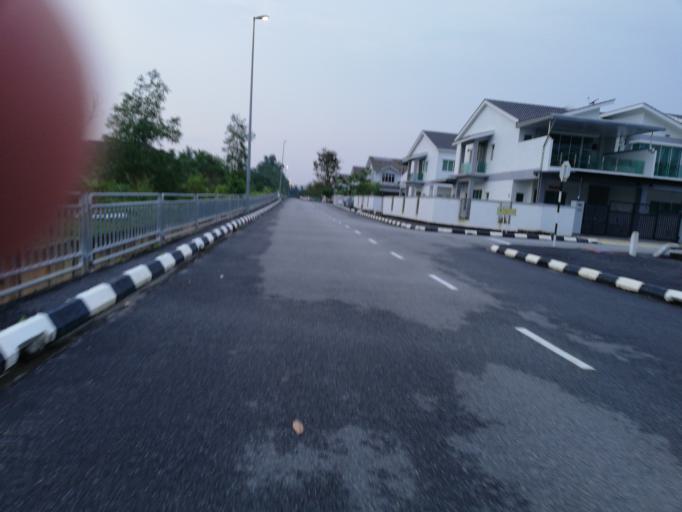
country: MY
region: Kedah
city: Kulim
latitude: 5.3834
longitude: 100.5810
